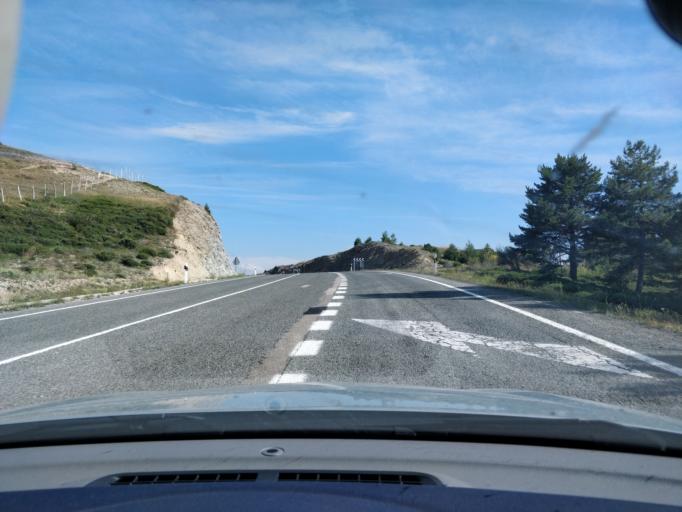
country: ES
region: Castille and Leon
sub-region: Provincia de Burgos
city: Espinosa de los Monteros
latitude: 42.9391
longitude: -3.6719
